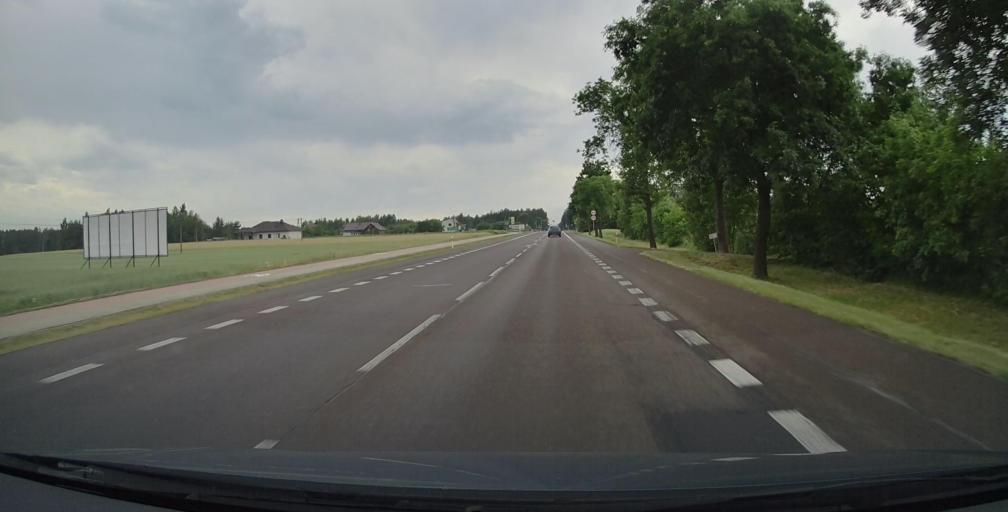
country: PL
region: Lublin Voivodeship
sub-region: Powiat bialski
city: Lesna Podlaska
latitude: 52.0360
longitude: 23.0099
